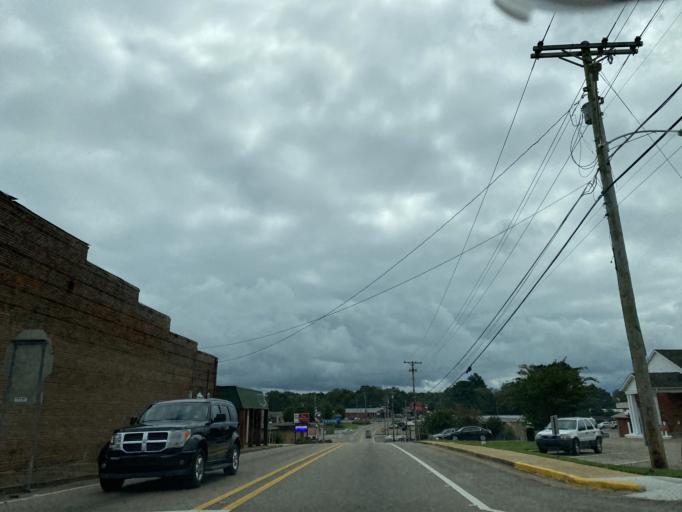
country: US
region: Mississippi
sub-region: Tishomingo County
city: Belmont
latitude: 34.5092
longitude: -88.2089
